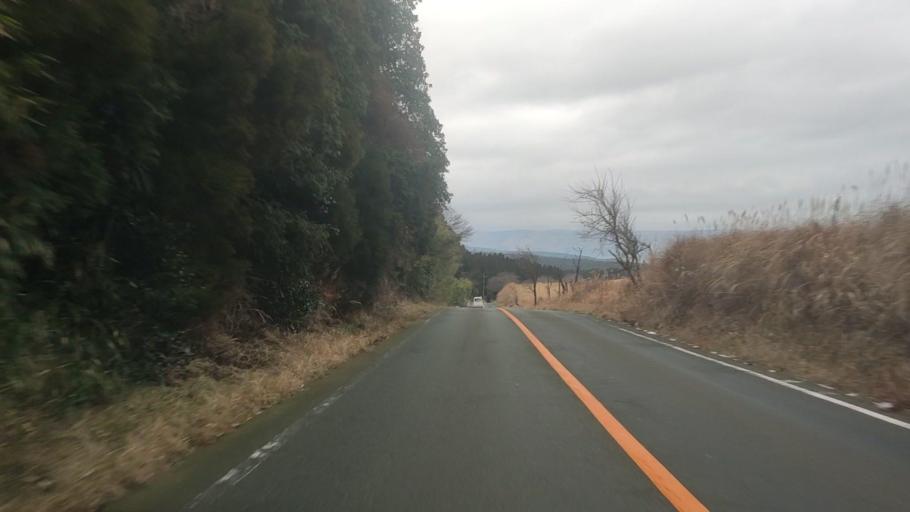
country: JP
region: Kumamoto
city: Aso
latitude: 32.9091
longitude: 131.1374
